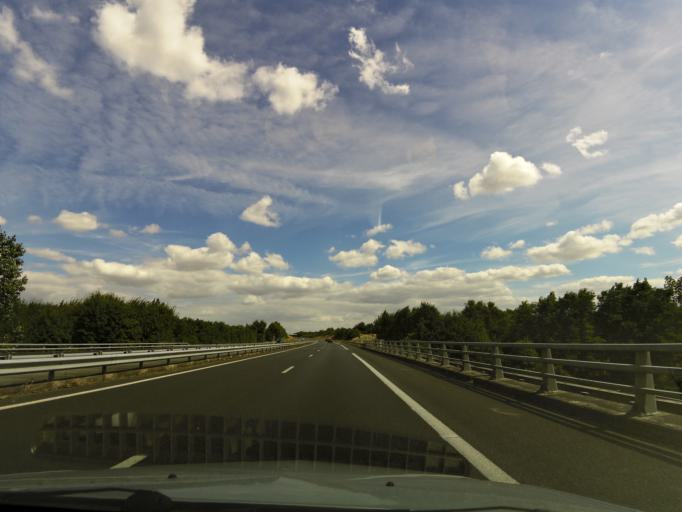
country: FR
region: Pays de la Loire
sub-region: Departement de la Vendee
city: Chauche
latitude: 46.8459
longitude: -1.2637
